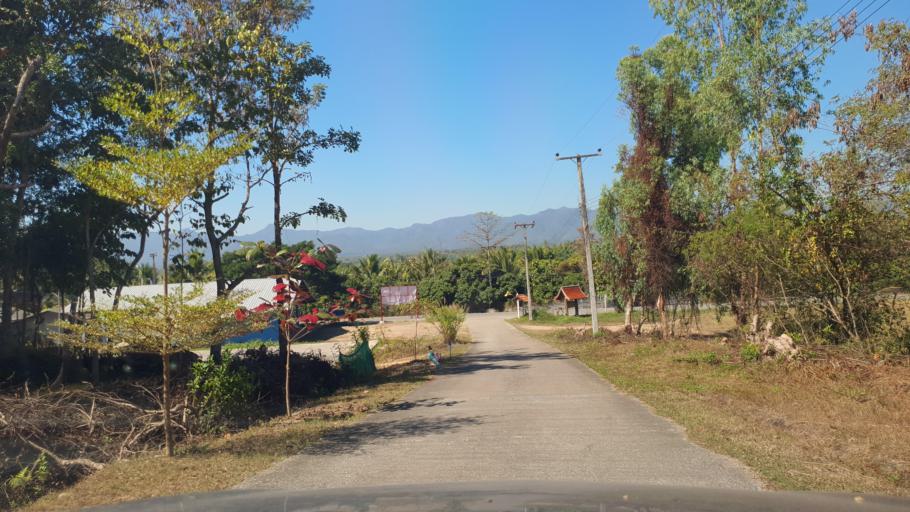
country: TH
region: Chiang Mai
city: San Pa Tong
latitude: 18.6536
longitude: 98.8381
